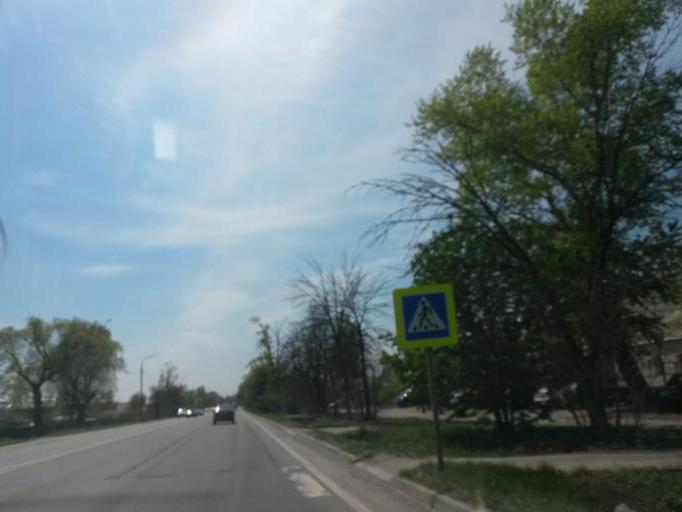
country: RU
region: Moskovskaya
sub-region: Podol'skiy Rayon
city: Podol'sk
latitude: 55.3941
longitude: 37.5462
